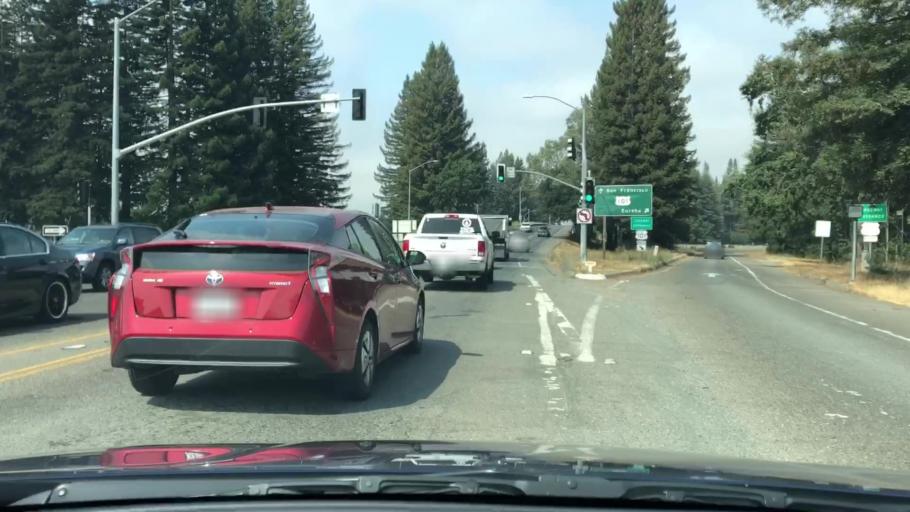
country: US
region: California
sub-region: Sonoma County
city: Larkfield-Wikiup
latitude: 38.4963
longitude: -122.7533
